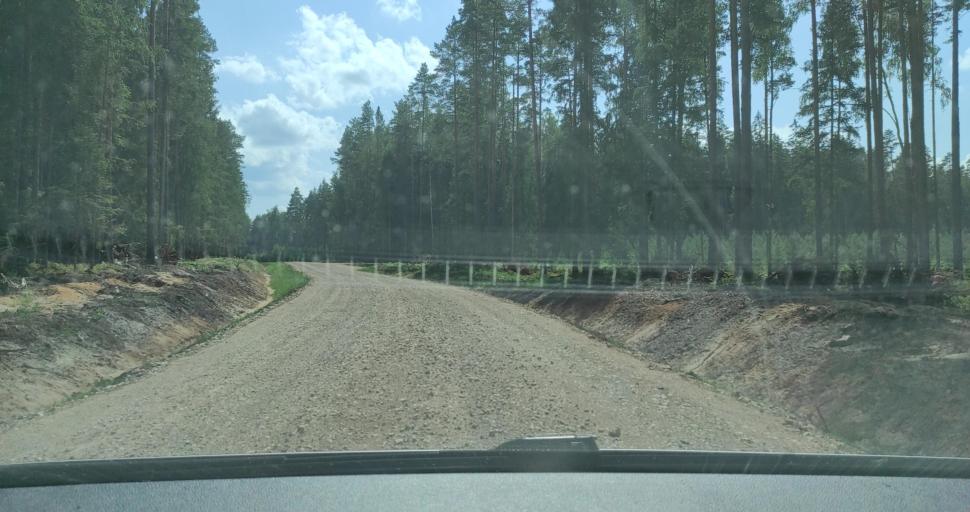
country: LV
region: Kuldigas Rajons
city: Kuldiga
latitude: 57.0662
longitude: 22.1927
